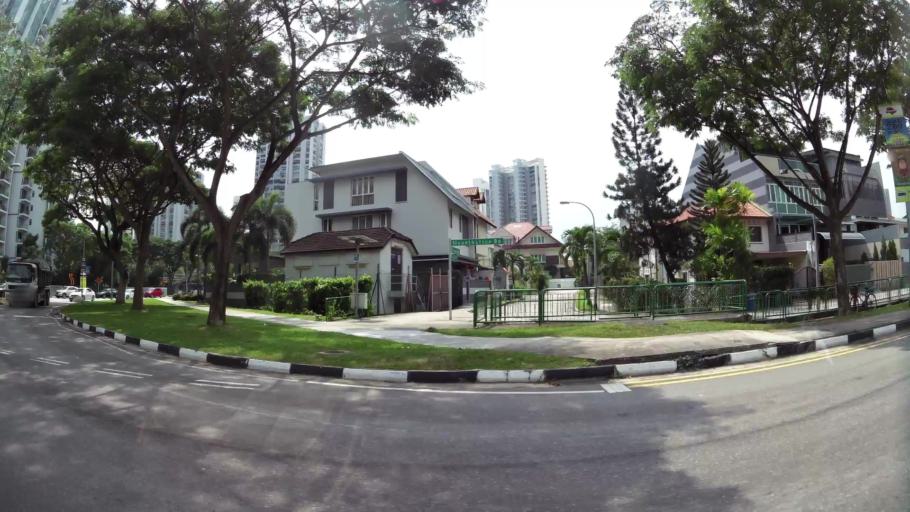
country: SG
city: Singapore
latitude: 1.3018
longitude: 103.8966
